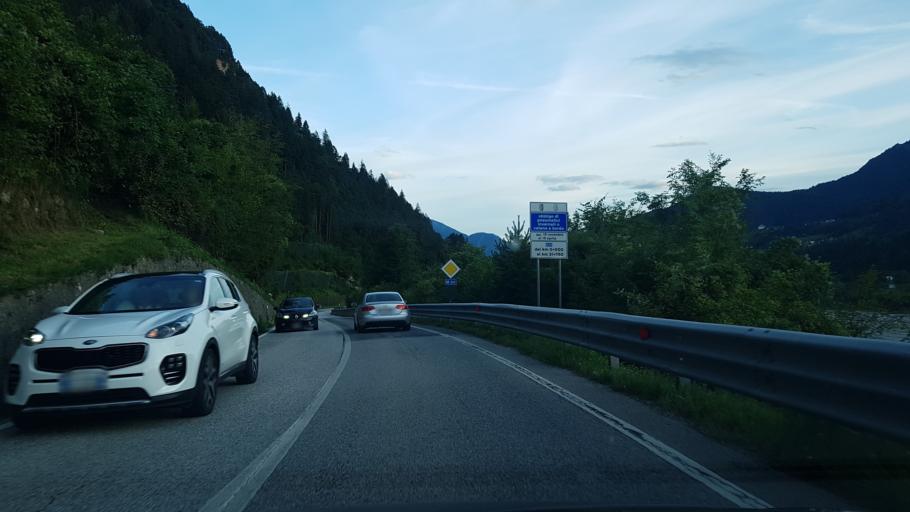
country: IT
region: Friuli Venezia Giulia
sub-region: Provincia di Udine
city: Comeglians
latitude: 46.5052
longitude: 12.8649
